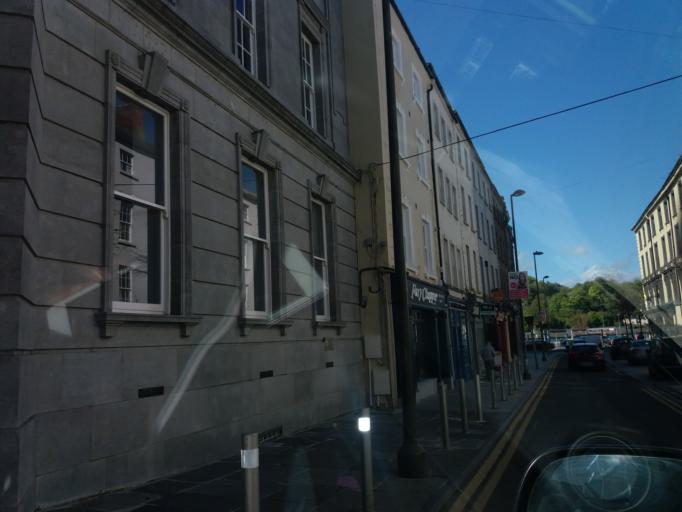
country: IE
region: Munster
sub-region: Waterford
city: Waterford
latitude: 52.2619
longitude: -7.1137
